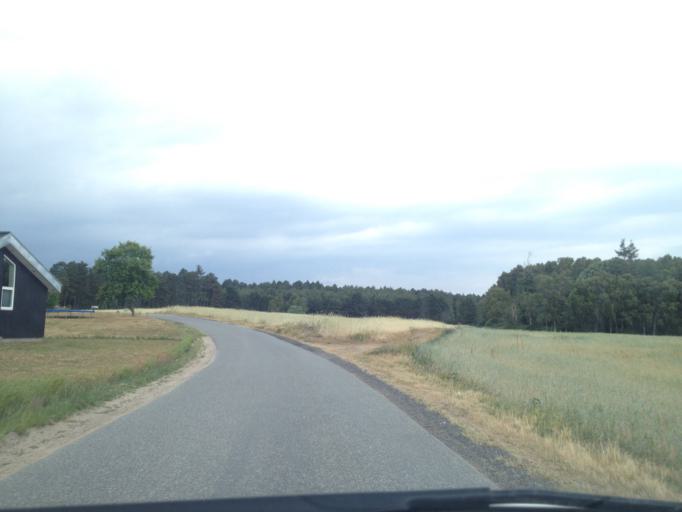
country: DK
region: Central Jutland
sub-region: Syddjurs Kommune
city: Ebeltoft
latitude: 56.1591
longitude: 10.6928
